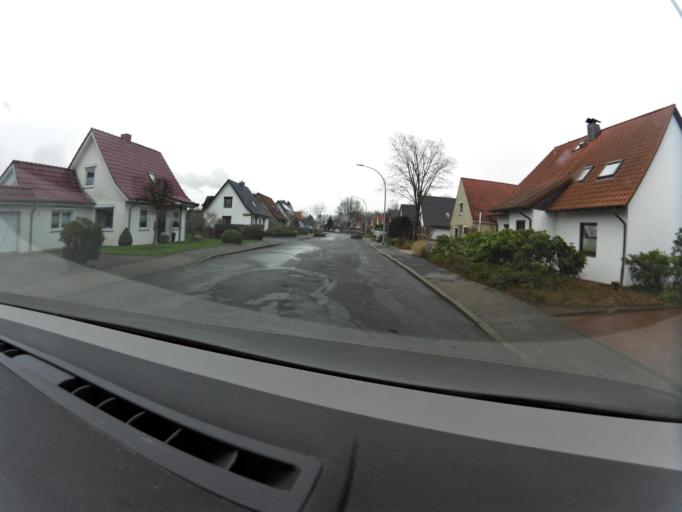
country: DE
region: Bremen
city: Bremerhaven
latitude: 53.5435
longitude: 8.5989
